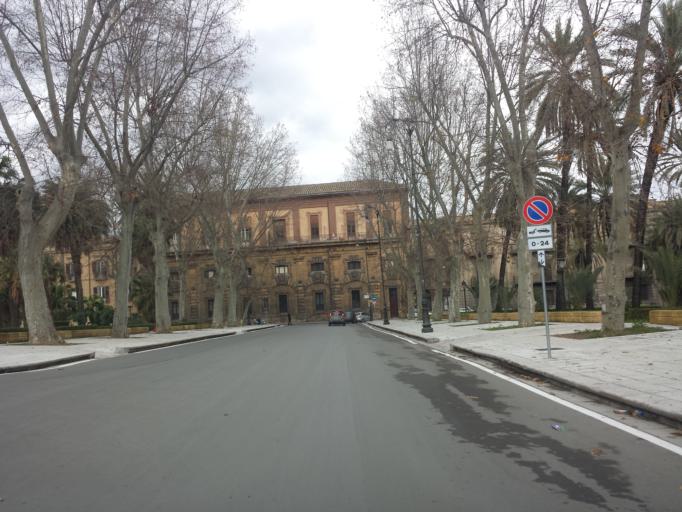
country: IT
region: Sicily
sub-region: Palermo
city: Palermo
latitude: 38.1120
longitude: 13.3545
